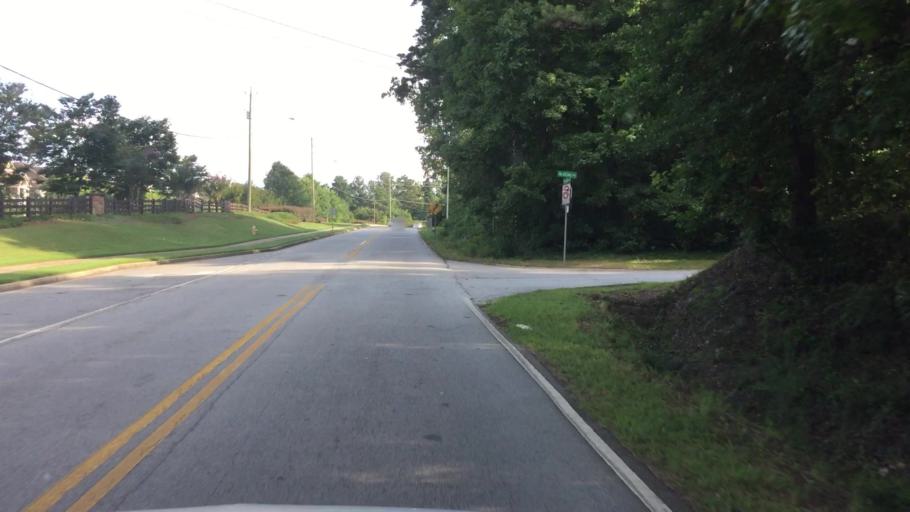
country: US
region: Georgia
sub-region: DeKalb County
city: Lithonia
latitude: 33.6963
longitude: -84.1085
